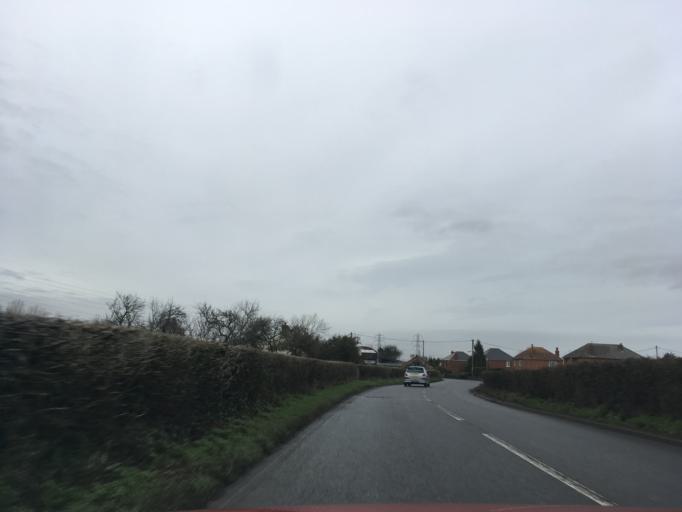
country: GB
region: Wales
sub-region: Newport
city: Nash
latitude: 51.5541
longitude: -2.9426
